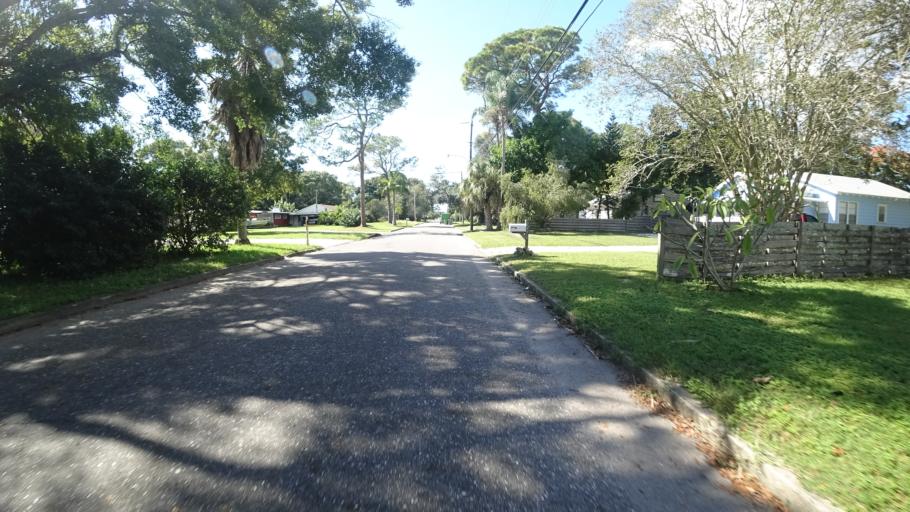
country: US
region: Florida
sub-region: Manatee County
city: South Bradenton
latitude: 27.4819
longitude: -82.5852
